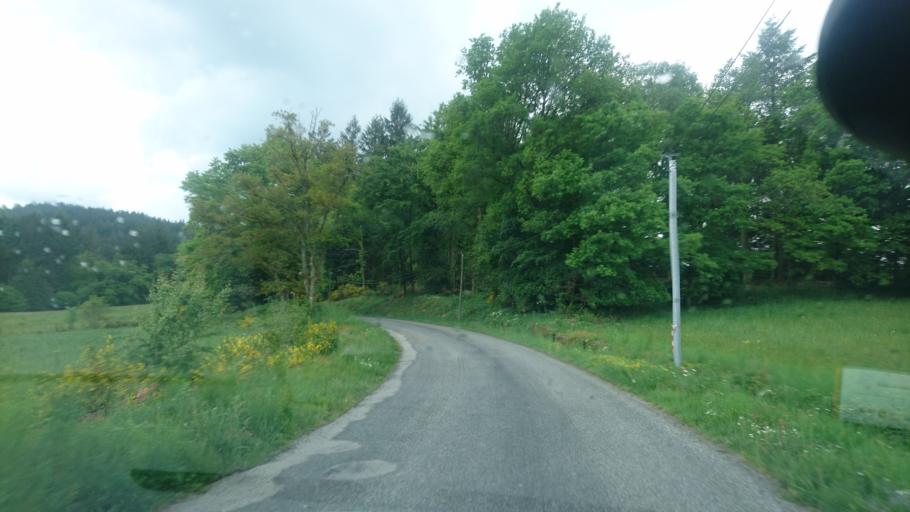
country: FR
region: Limousin
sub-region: Departement de la Haute-Vienne
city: Peyrat-le-Chateau
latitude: 45.8329
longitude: 1.8664
